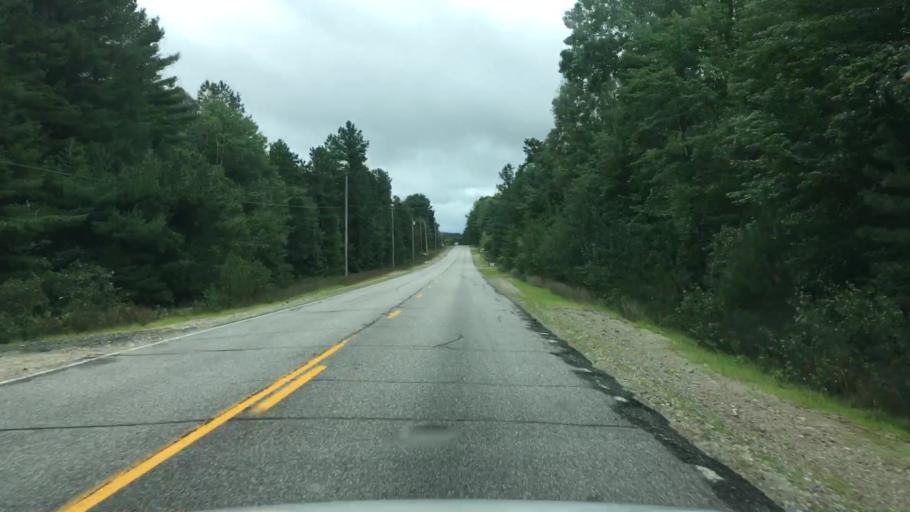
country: US
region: Maine
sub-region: Oxford County
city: Hiram
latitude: 43.9034
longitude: -70.8418
